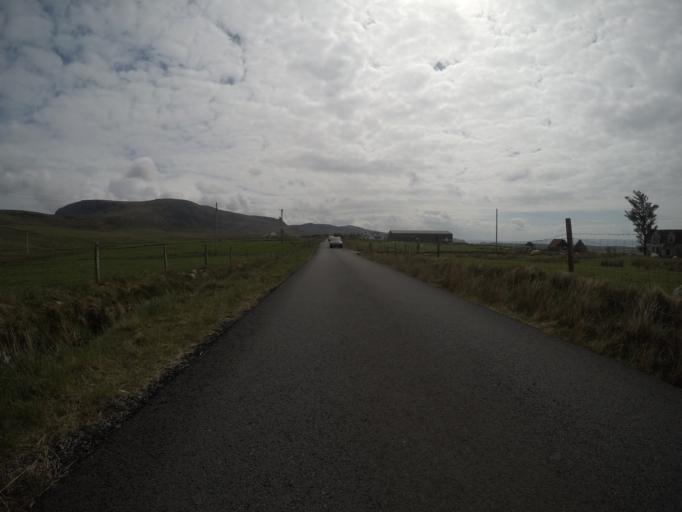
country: GB
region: Scotland
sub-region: Highland
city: Portree
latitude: 57.6451
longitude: -6.3786
